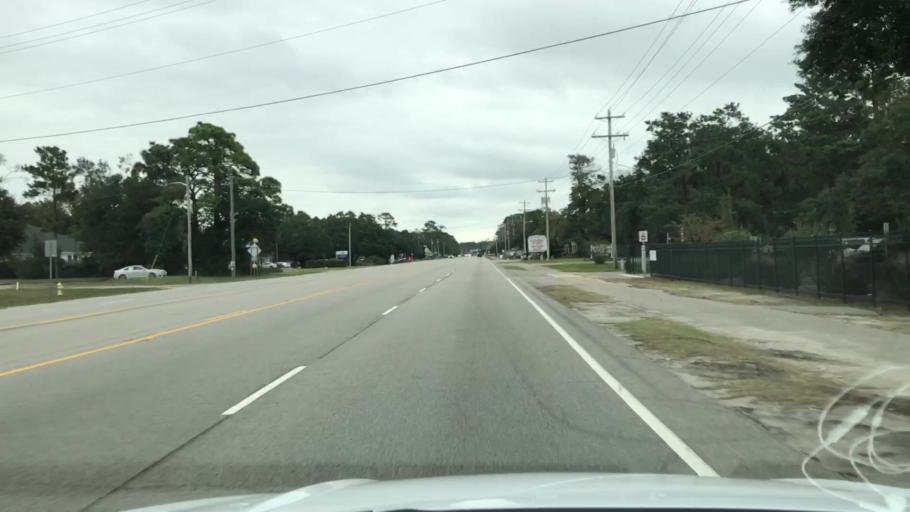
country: US
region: South Carolina
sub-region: Georgetown County
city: Murrells Inlet
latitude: 33.4321
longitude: -79.1411
